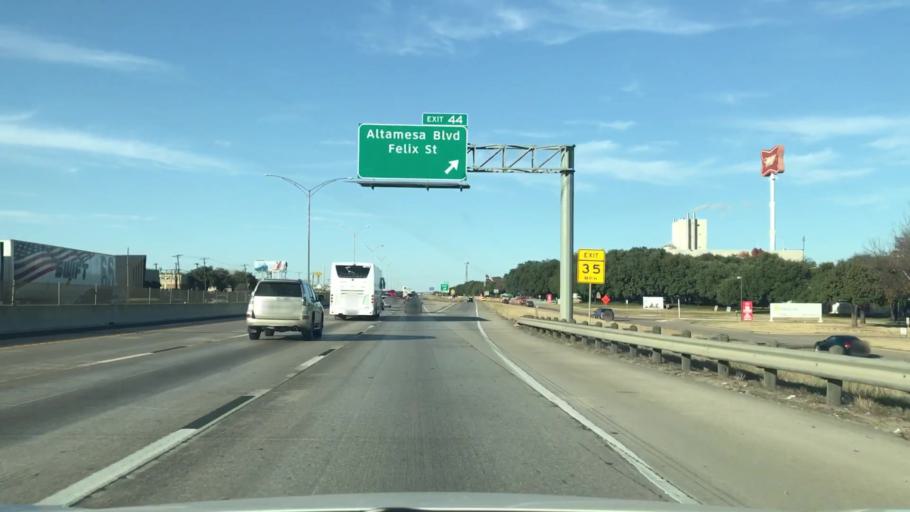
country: US
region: Texas
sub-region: Tarrant County
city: Edgecliff Village
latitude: 32.6381
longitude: -97.3215
